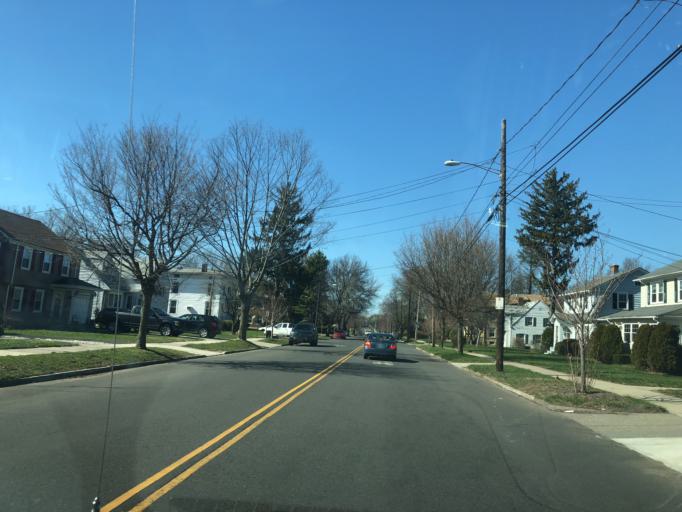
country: US
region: Connecticut
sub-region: Hartford County
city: Hartford
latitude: 41.7291
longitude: -72.6914
